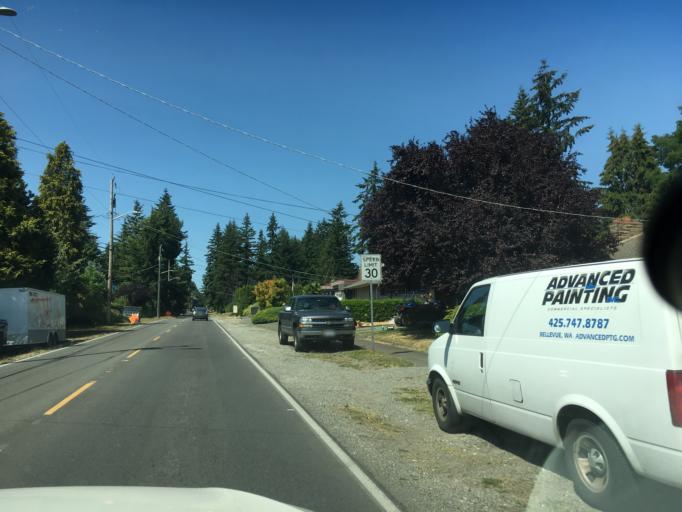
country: US
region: Washington
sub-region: King County
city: Shoreline
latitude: 47.7201
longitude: -122.3609
